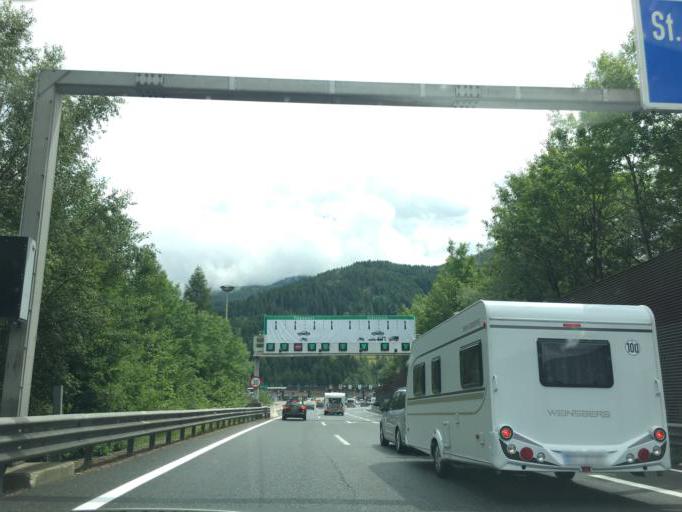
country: AT
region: Salzburg
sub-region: Politischer Bezirk Tamsweg
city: Sankt Michael im Lungau
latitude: 47.0959
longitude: 13.6080
